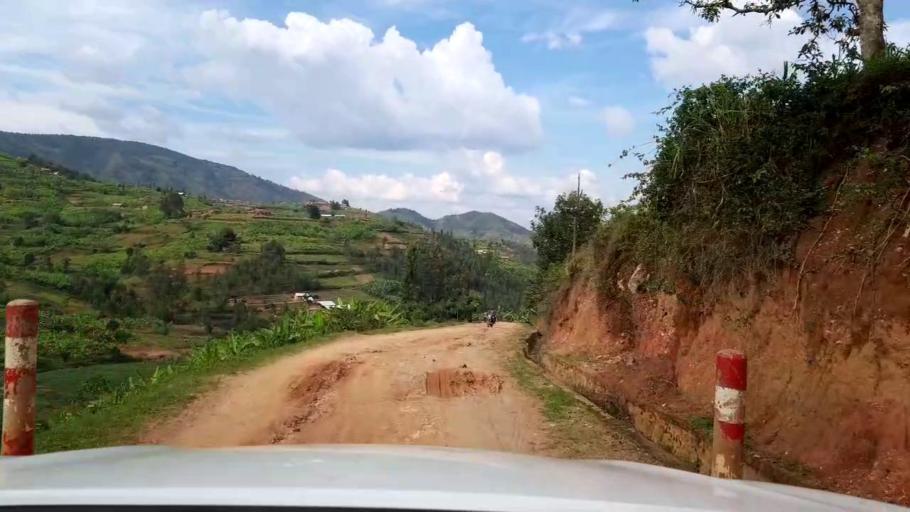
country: RW
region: Southern Province
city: Gitarama
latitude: -1.9765
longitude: 29.7087
